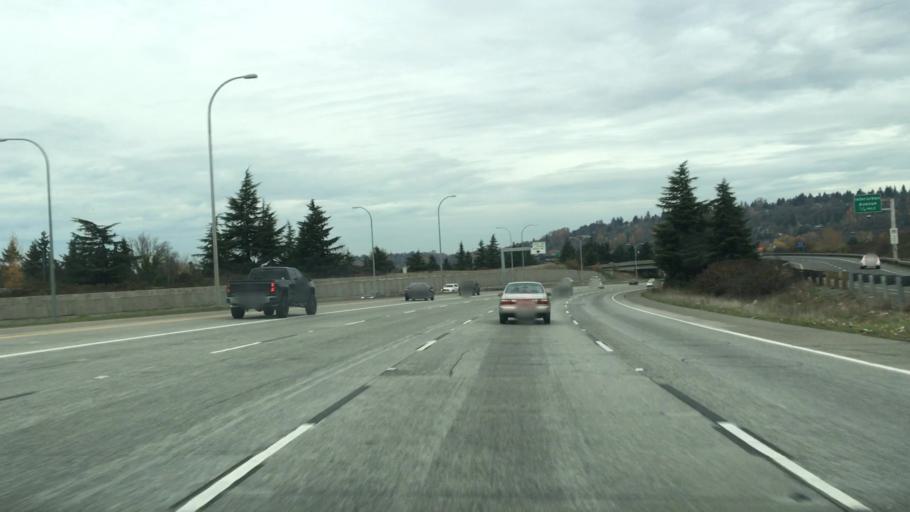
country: US
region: Washington
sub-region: King County
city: Tukwila
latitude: 47.4795
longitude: -122.2716
